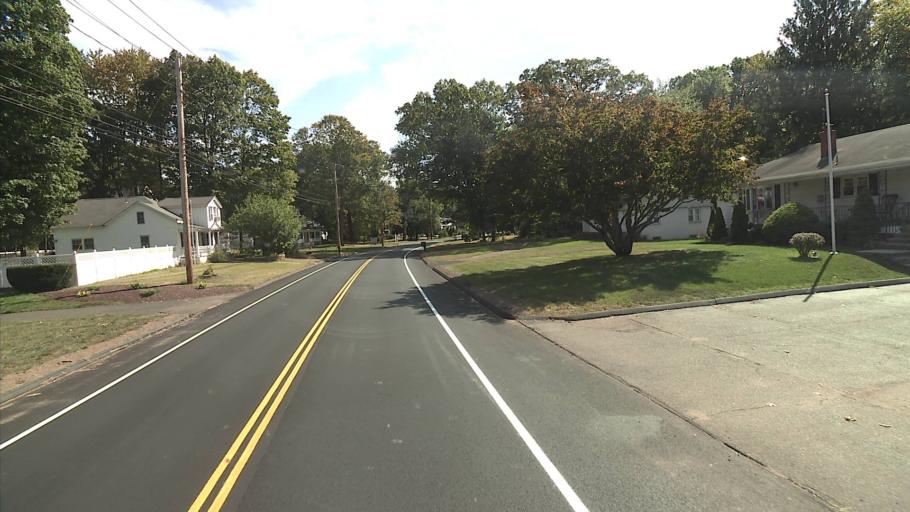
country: US
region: Connecticut
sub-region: New Haven County
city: North Haven
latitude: 41.3757
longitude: -72.8528
